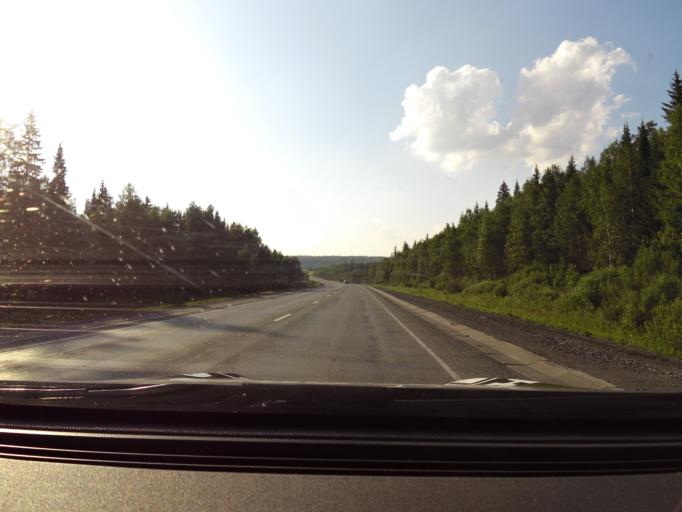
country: RU
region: Sverdlovsk
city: Revda
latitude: 56.8423
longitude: 59.8247
